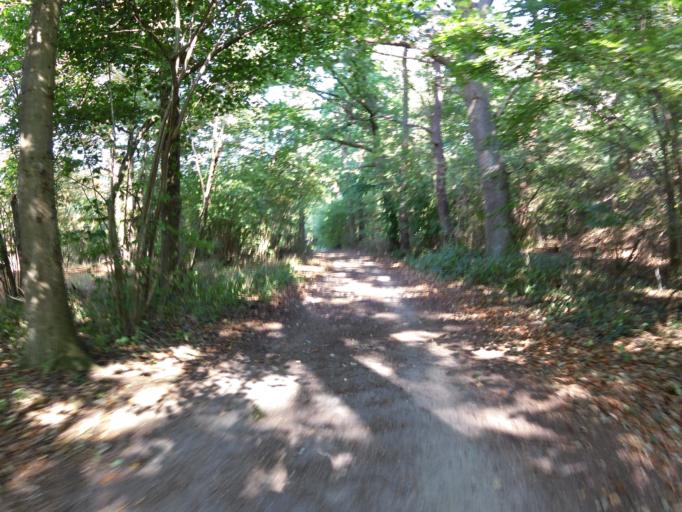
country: DE
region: Mecklenburg-Vorpommern
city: Loddin
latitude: 53.9653
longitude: 14.0444
